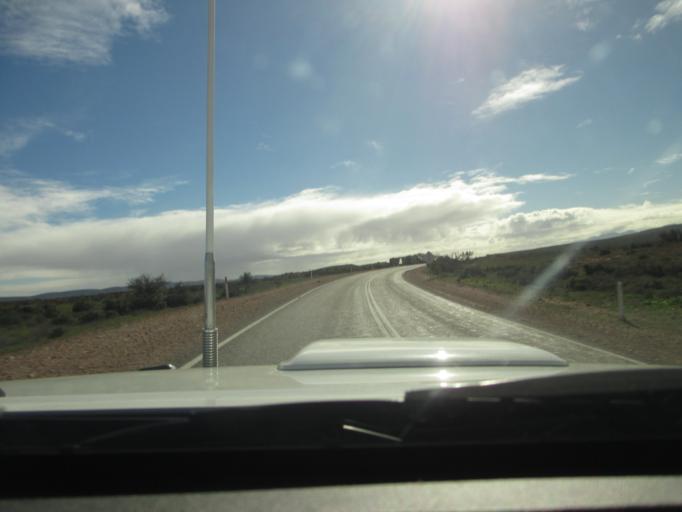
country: AU
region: South Australia
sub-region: Flinders Ranges
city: Quorn
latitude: -31.7593
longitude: 138.3315
